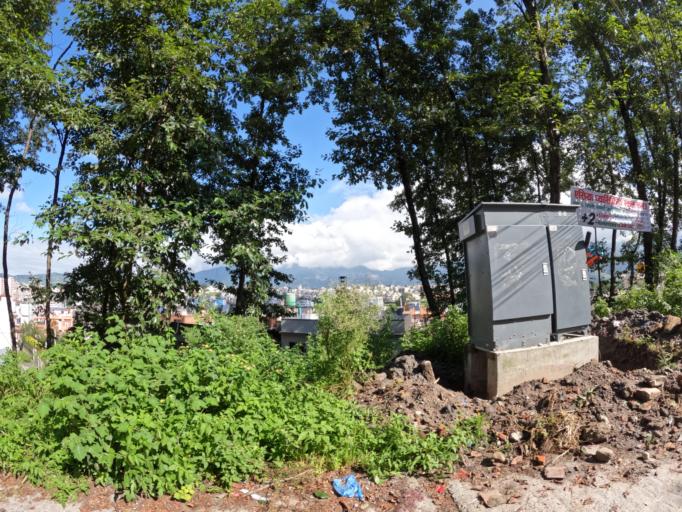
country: NP
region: Central Region
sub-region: Bagmati Zone
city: Kathmandu
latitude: 27.7544
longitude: 85.3320
